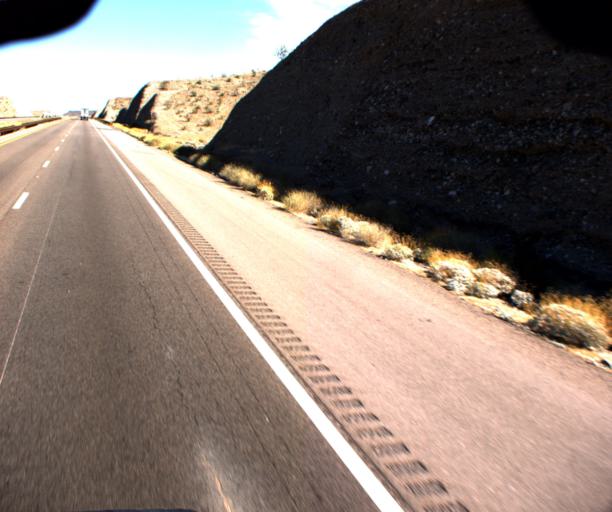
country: US
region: Nevada
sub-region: Clark County
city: Boulder City
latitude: 35.9027
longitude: -114.6269
